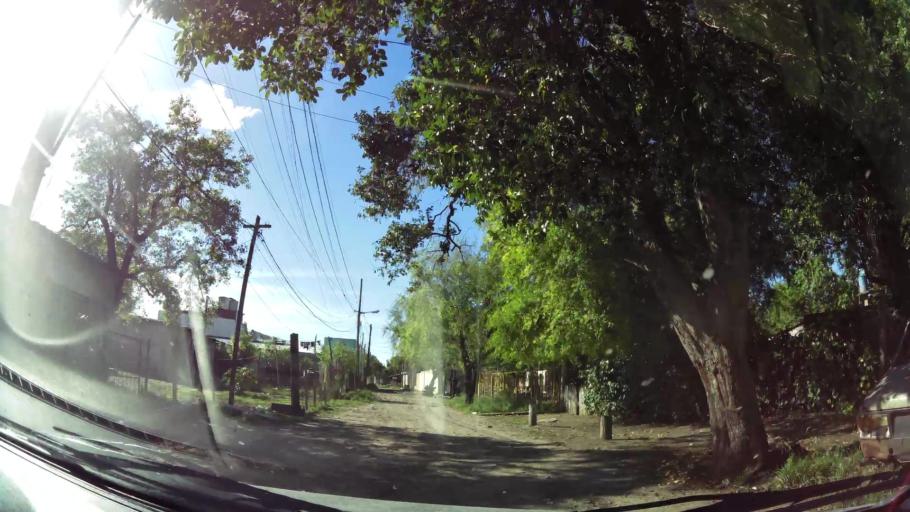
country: AR
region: Buenos Aires
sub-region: Partido de Almirante Brown
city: Adrogue
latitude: -34.8254
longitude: -58.3419
